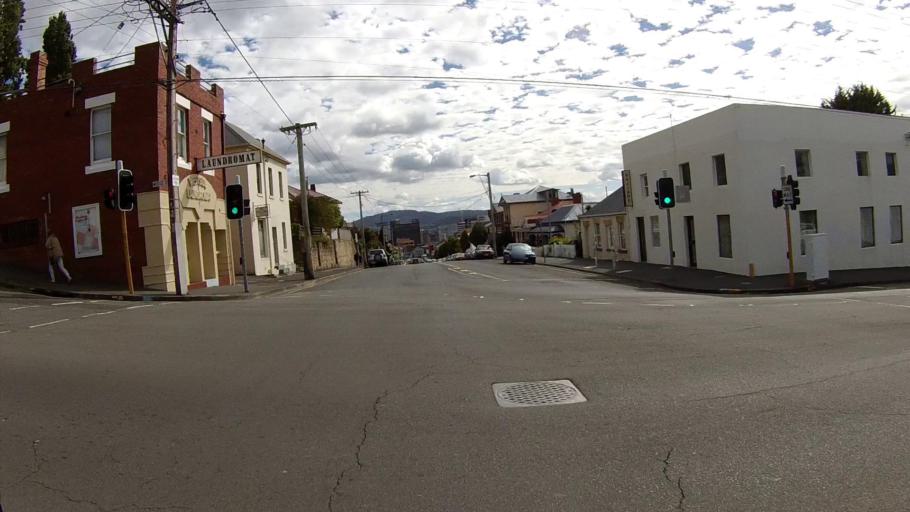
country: AU
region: Tasmania
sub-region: Hobart
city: Sandy Bay
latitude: -42.8865
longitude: 147.3196
